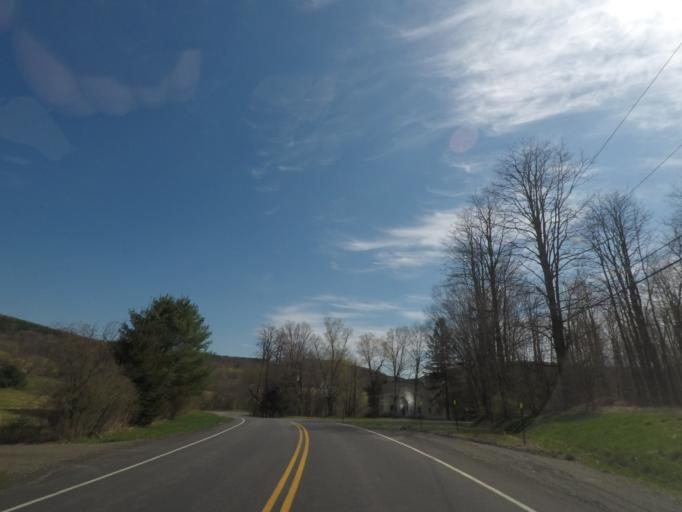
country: US
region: New York
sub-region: Columbia County
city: Chatham
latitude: 42.3850
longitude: -73.5309
